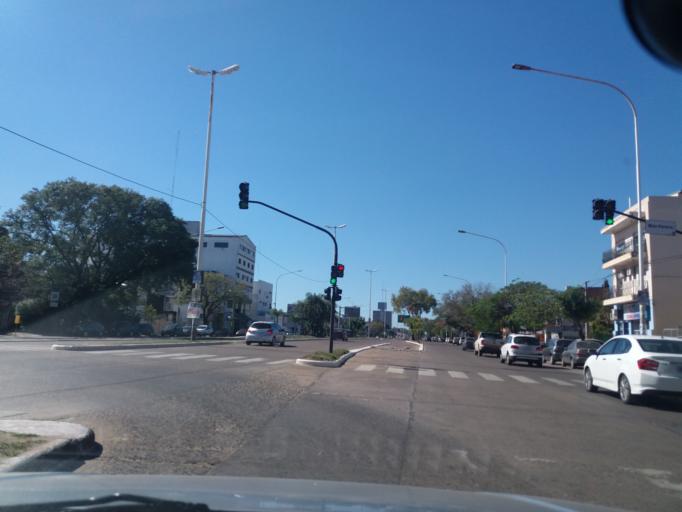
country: AR
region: Corrientes
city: Corrientes
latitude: -27.4753
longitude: -58.8413
